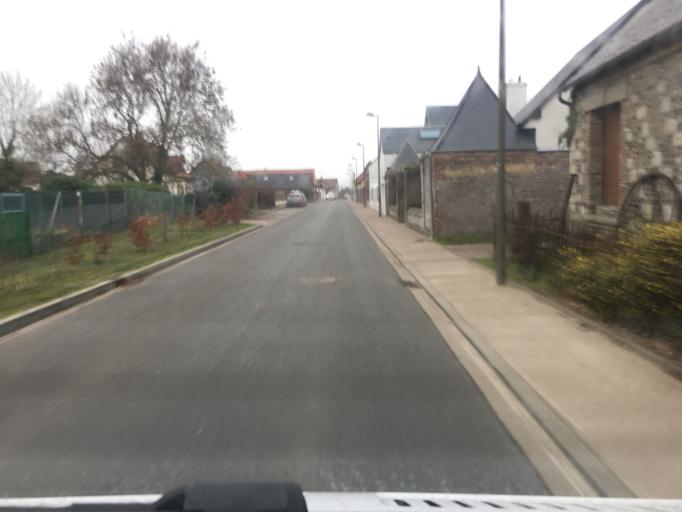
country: FR
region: Picardie
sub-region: Departement de la Somme
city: Saint-Valery-sur-Somme
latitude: 50.1803
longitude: 1.6339
